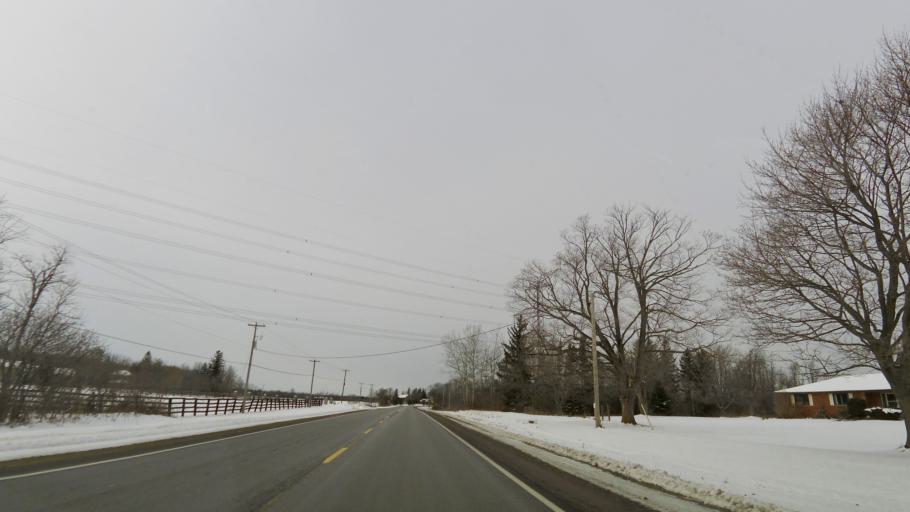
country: CA
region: Ontario
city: Ancaster
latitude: 43.2867
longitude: -80.0845
